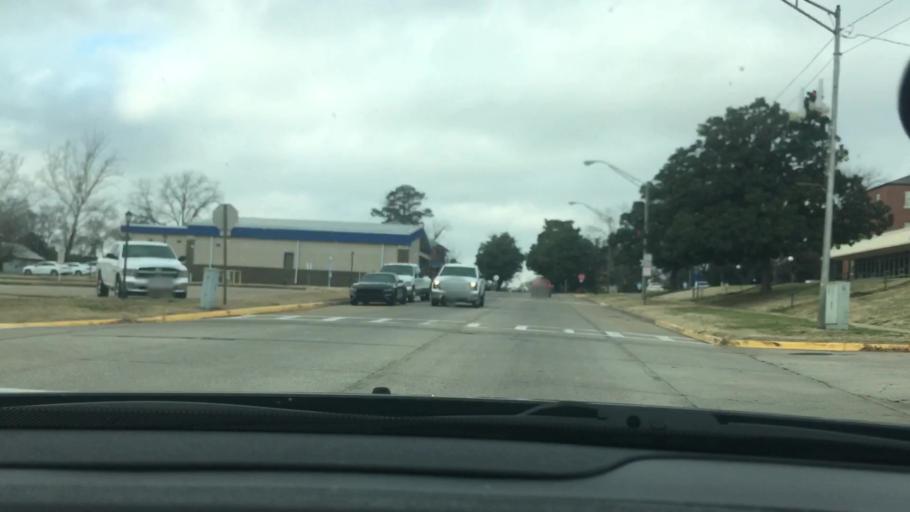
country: US
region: Oklahoma
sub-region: Bryan County
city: Durant
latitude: 34.0050
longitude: -96.3761
